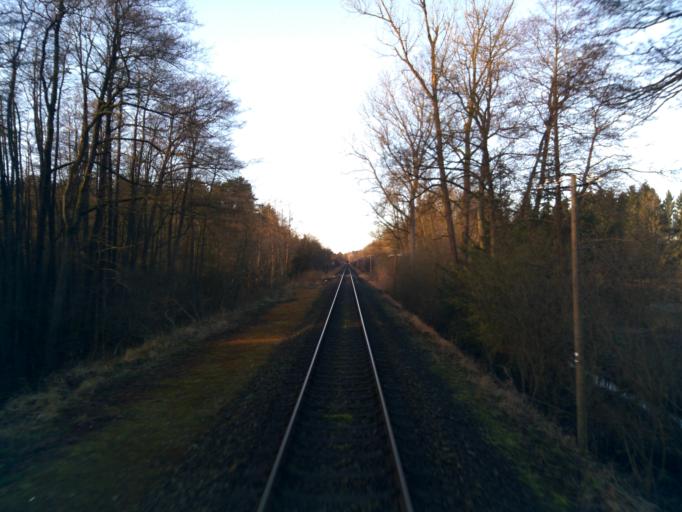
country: DE
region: Lower Saxony
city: Munster
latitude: 52.9993
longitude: 10.0184
